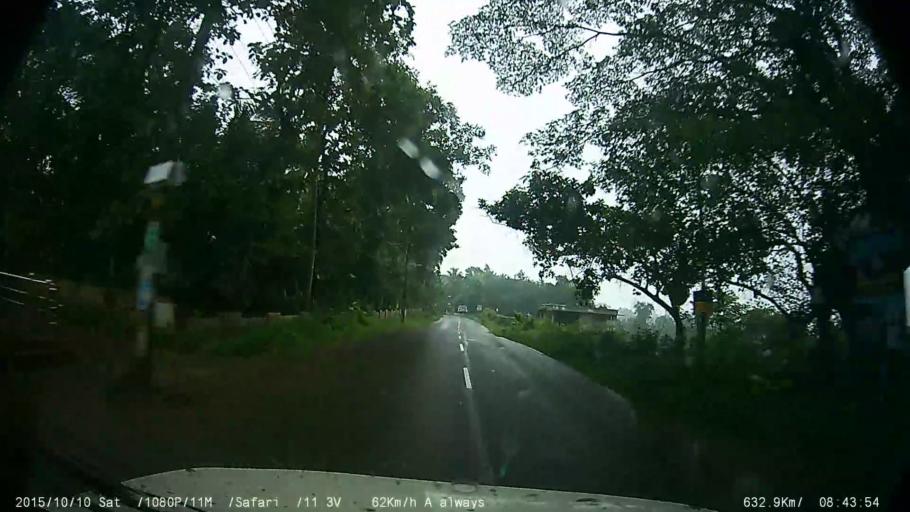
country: IN
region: Kerala
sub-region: Kottayam
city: Palackattumala
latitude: 9.7458
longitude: 76.5311
